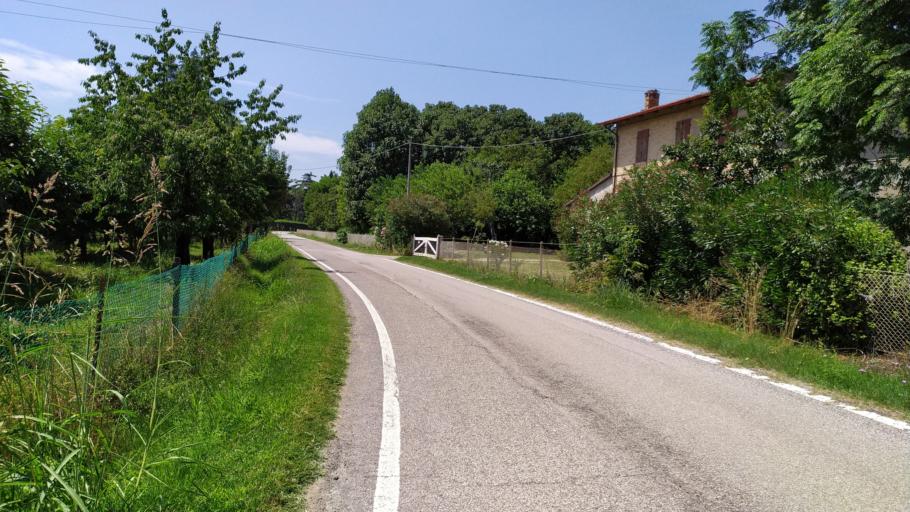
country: IT
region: Emilia-Romagna
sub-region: Forli-Cesena
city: Castrocaro Terme e Terra del Sole
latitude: 44.2005
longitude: 11.9850
